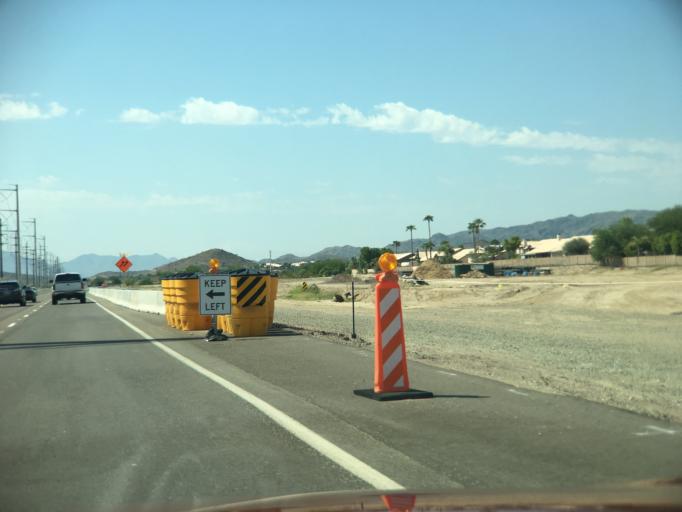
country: US
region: Arizona
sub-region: Maricopa County
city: Guadalupe
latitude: 33.2911
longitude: -112.0181
